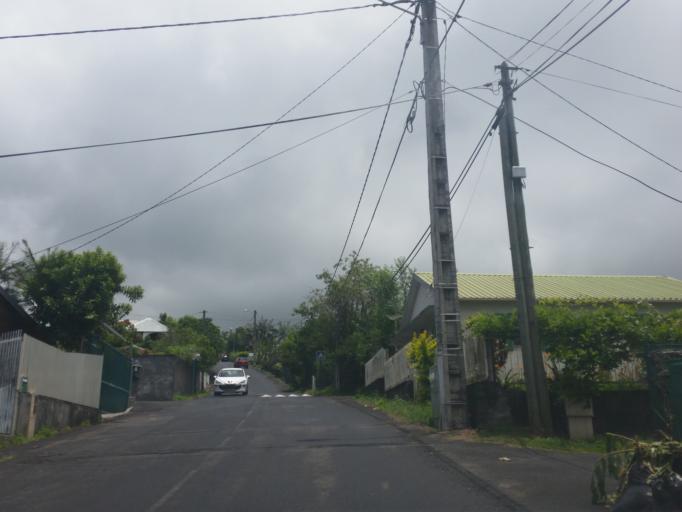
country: RE
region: Reunion
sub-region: Reunion
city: Le Tampon
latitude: -21.2460
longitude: 55.5117
